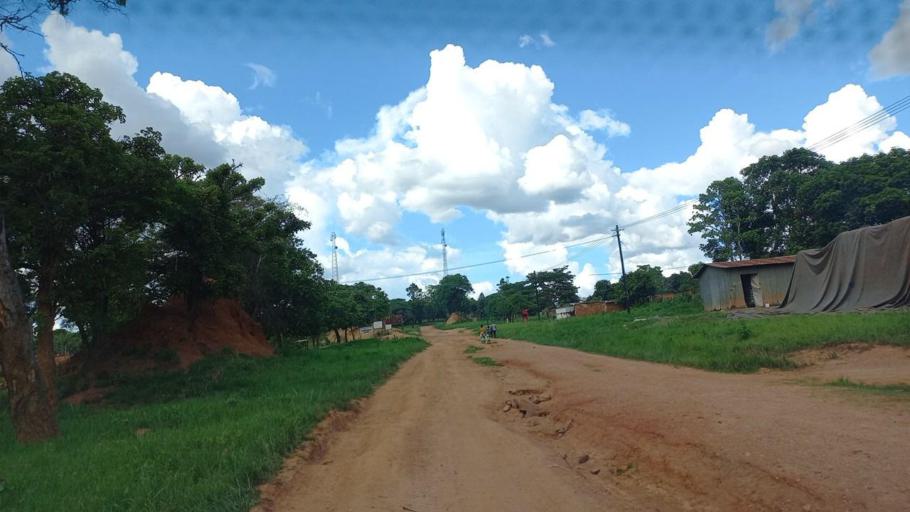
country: ZM
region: North-Western
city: Mwinilunga
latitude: -12.0712
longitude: 24.3011
